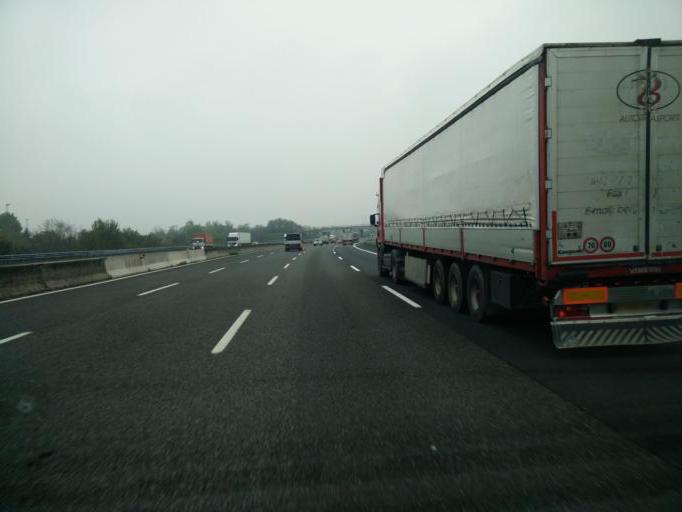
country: IT
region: Emilia-Romagna
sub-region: Provincia di Modena
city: Baggiovara
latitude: 44.6186
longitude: 10.8859
